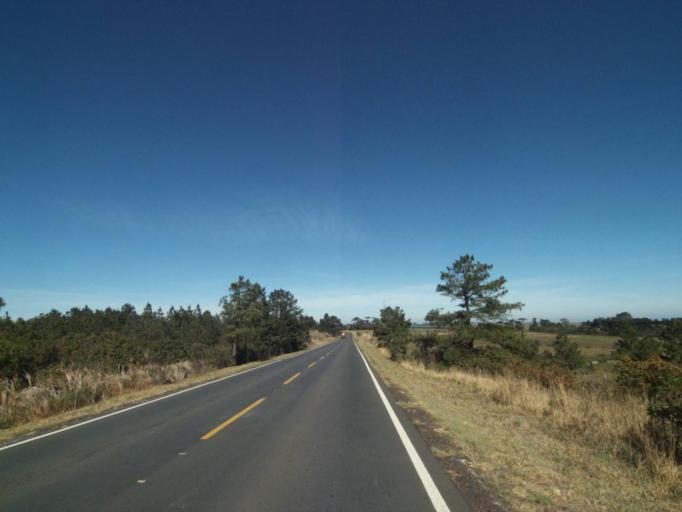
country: BR
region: Parana
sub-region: Castro
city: Castro
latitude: -24.7419
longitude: -50.1832
